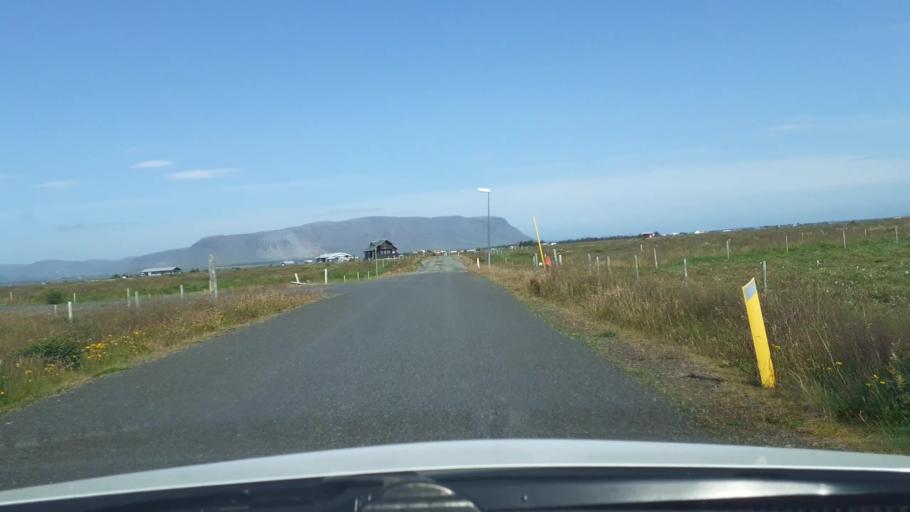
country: IS
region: South
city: Selfoss
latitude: 63.8957
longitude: -21.0809
